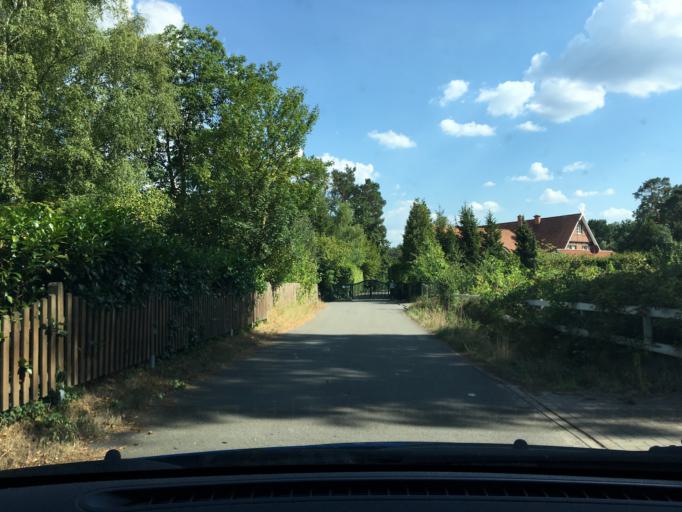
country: DE
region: Lower Saxony
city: Salzhausen
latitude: 53.2184
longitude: 10.2002
